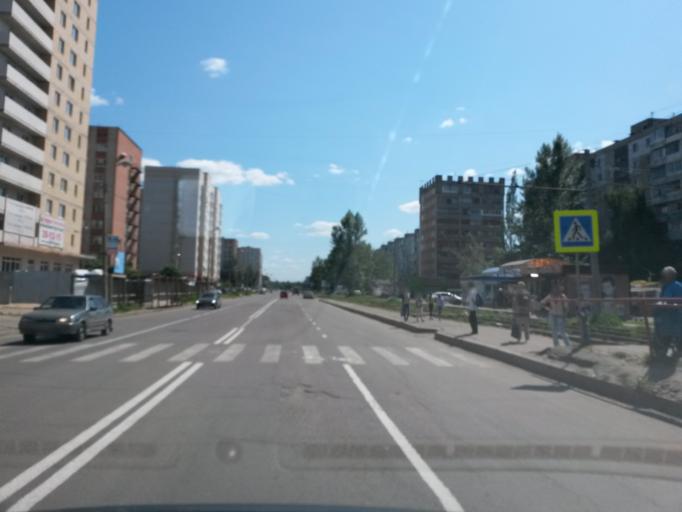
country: RU
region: Jaroslavl
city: Yaroslavl
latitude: 57.6904
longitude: 39.7588
